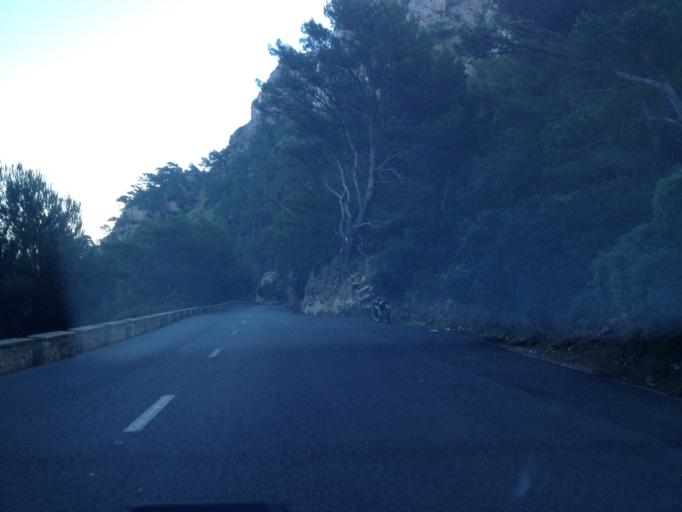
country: ES
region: Balearic Islands
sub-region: Illes Balears
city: Alcudia
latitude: 39.9293
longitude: 3.1122
